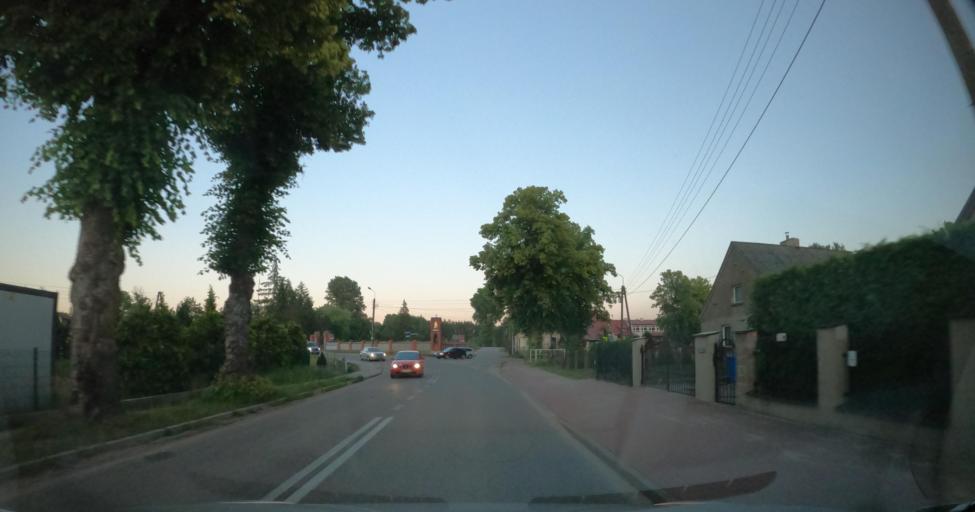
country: PL
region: Pomeranian Voivodeship
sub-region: Powiat wejherowski
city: Linia
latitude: 54.4545
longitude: 18.0292
